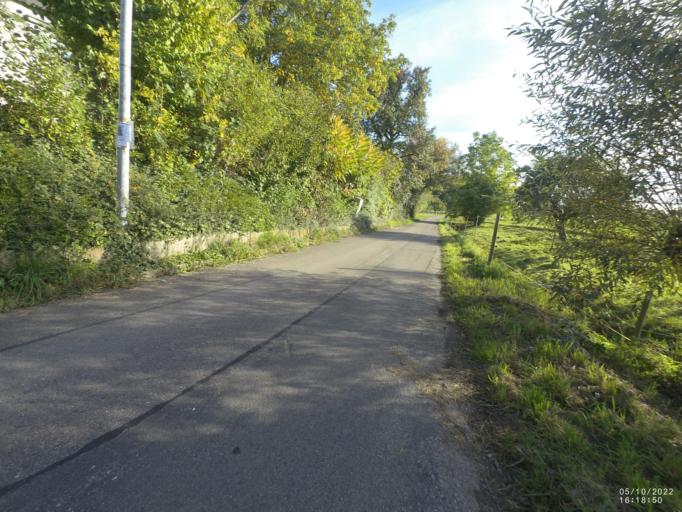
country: DE
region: Baden-Wuerttemberg
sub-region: Regierungsbezirk Stuttgart
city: Ebersbach an der Fils
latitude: 48.7015
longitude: 9.5046
